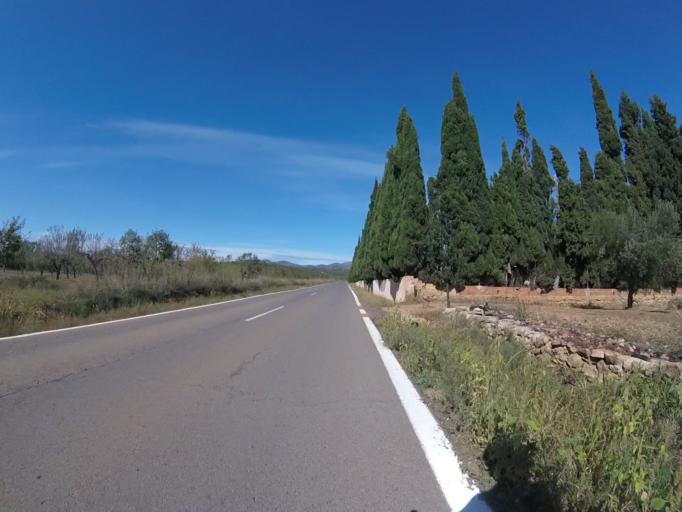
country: ES
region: Valencia
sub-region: Provincia de Castello
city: Benlloch
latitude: 40.2141
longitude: 0.0212
